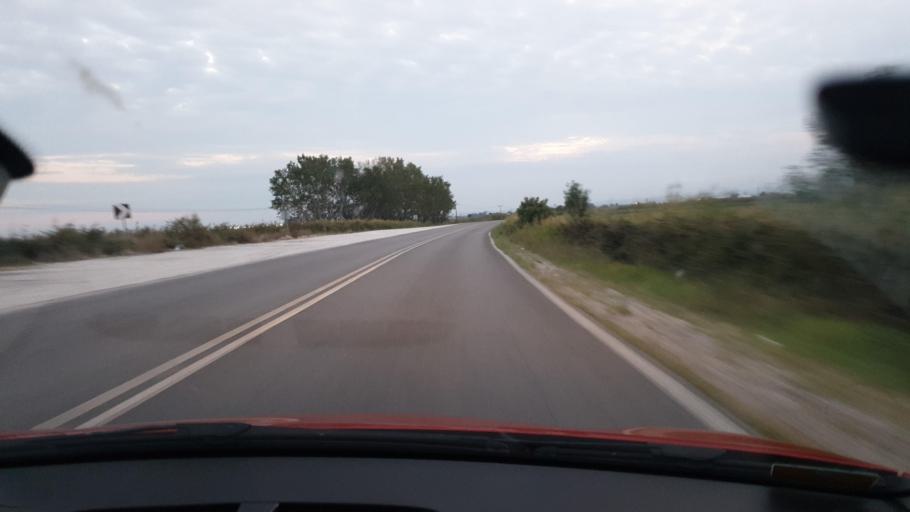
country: GR
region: Central Macedonia
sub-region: Nomos Kilkis
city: Polykastro
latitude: 41.0018
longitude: 22.6359
